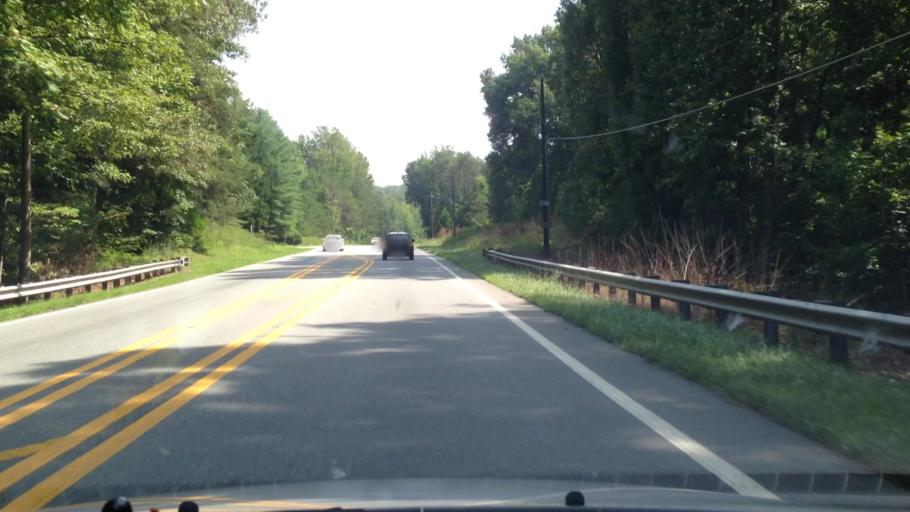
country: US
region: North Carolina
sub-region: Guilford County
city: Oak Ridge
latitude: 36.2045
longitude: -79.9869
